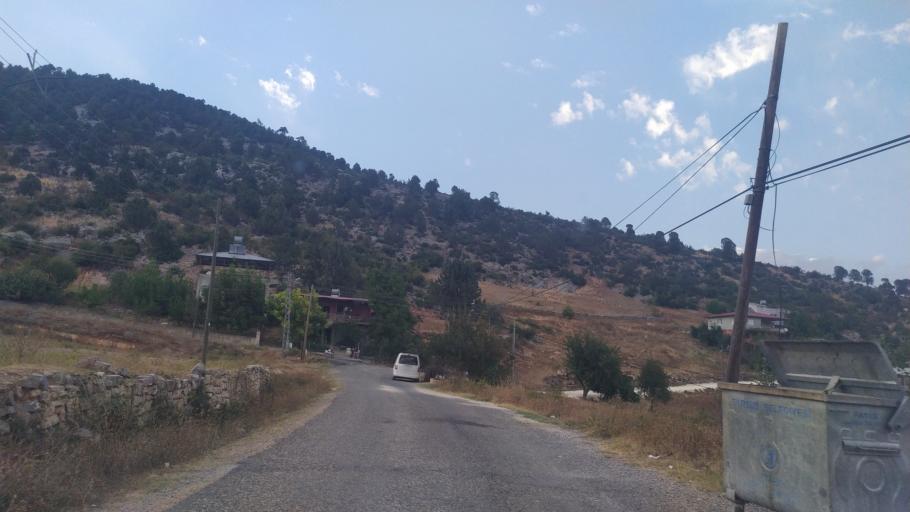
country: TR
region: Mersin
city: Camliyayla
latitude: 37.2298
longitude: 34.7102
